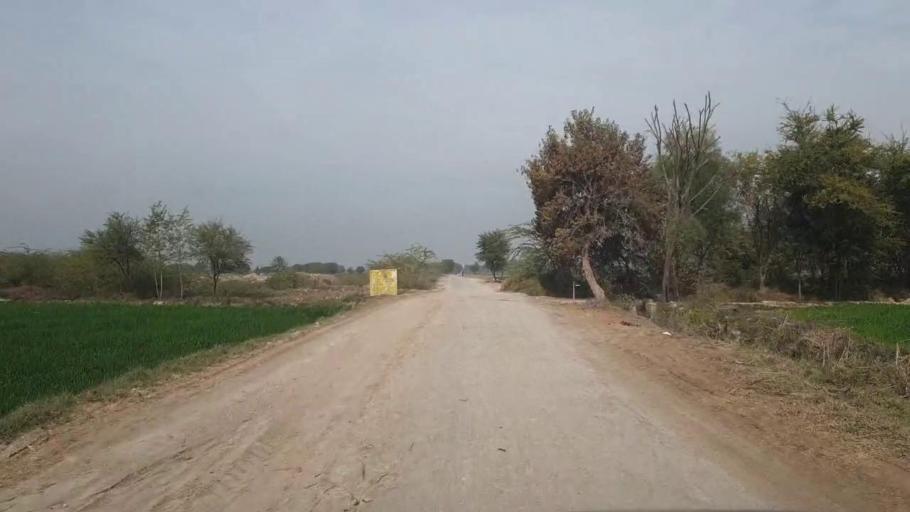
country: PK
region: Sindh
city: Nawabshah
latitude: 26.1147
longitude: 68.4800
